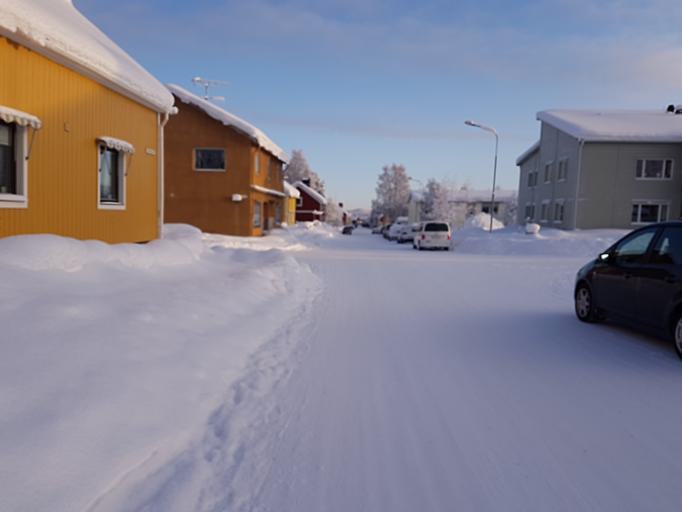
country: SE
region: Norrbotten
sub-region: Jokkmokks Kommun
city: Jokkmokk
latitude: 66.6083
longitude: 19.8207
